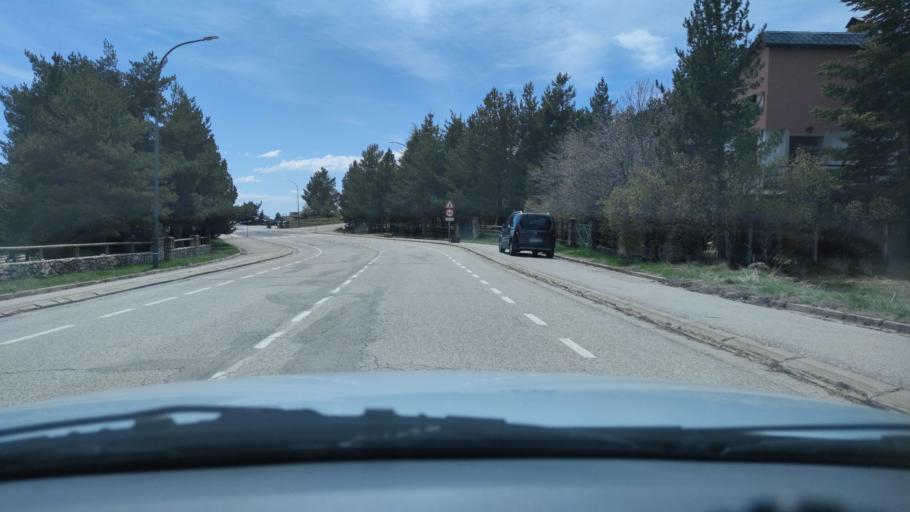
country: ES
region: Catalonia
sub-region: Provincia de Lleida
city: Gosol
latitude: 42.1703
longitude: 1.5698
